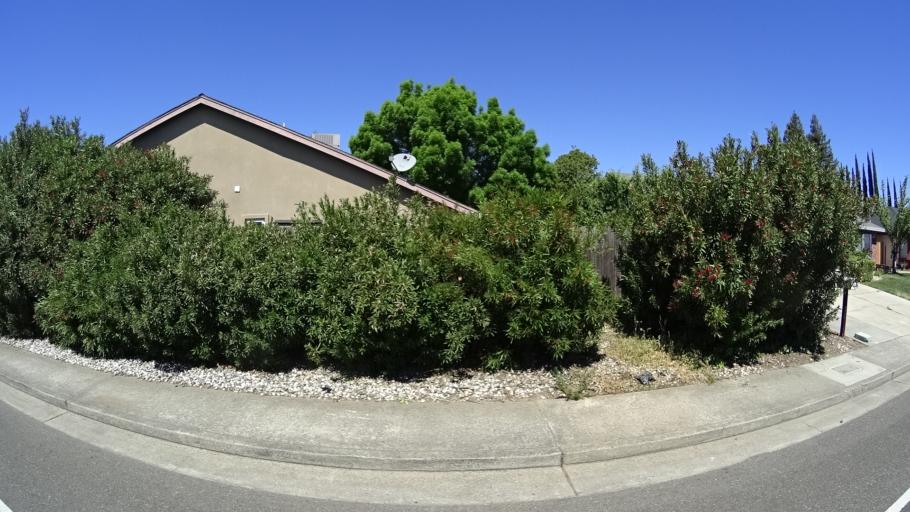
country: US
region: California
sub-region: Placer County
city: Rocklin
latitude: 38.7938
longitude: -121.2196
